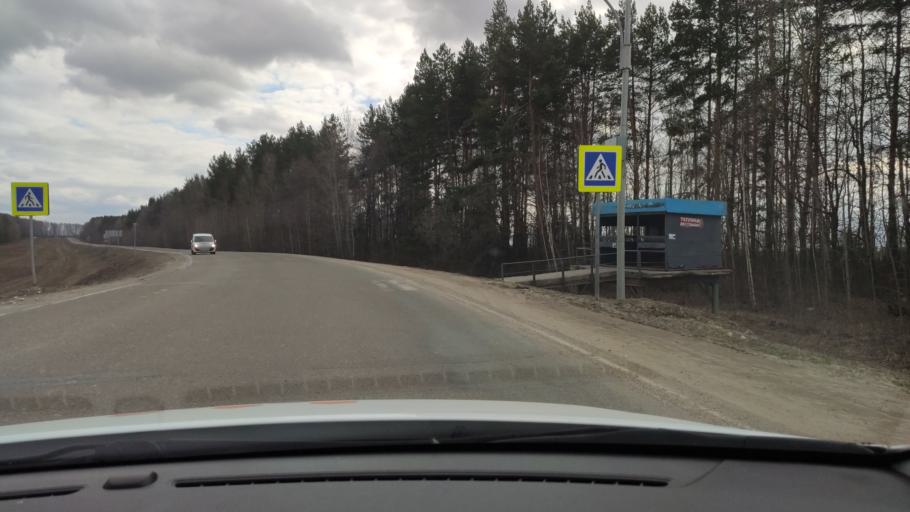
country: RU
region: Tatarstan
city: Vysokaya Gora
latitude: 56.1035
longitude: 49.1799
